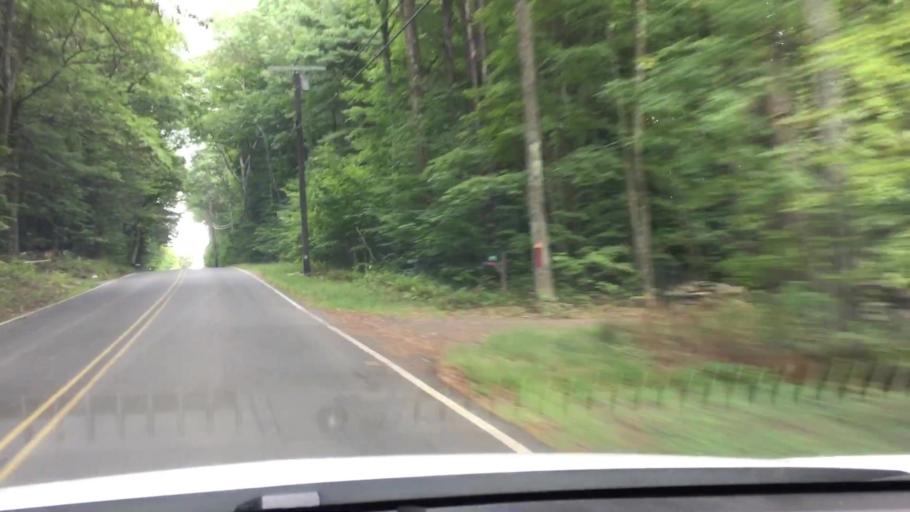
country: US
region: Massachusetts
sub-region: Berkshire County
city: Otis
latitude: 42.2171
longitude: -72.9524
